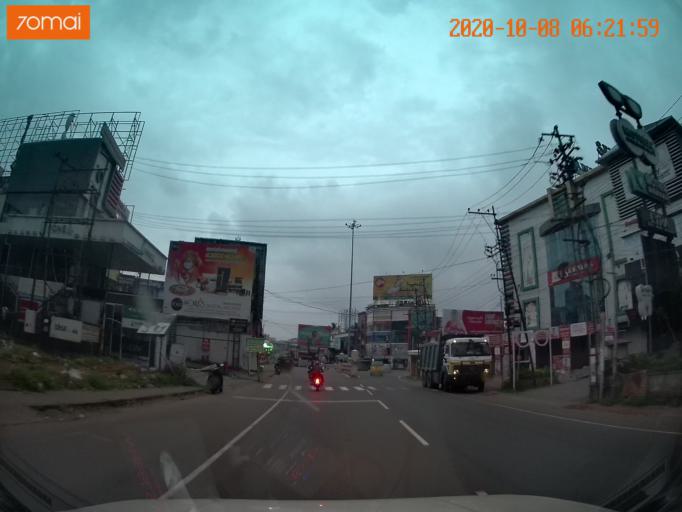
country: IN
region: Kerala
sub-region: Thrissur District
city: Trichur
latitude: 10.5227
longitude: 76.2264
